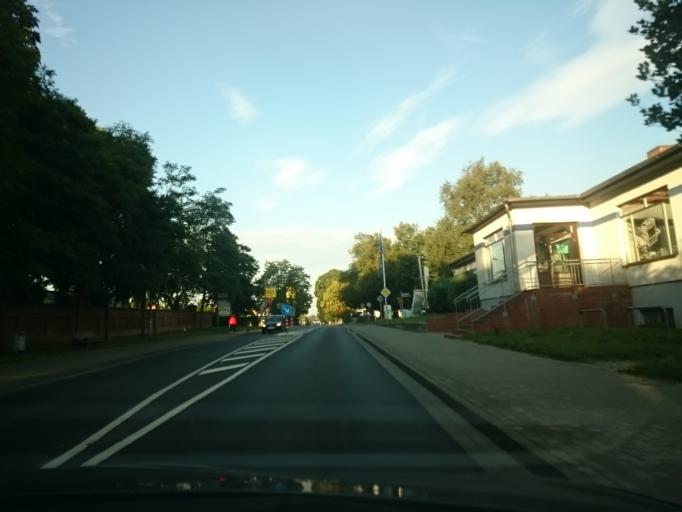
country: DE
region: Mecklenburg-Vorpommern
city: Wolgast
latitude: 54.0517
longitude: 13.7697
